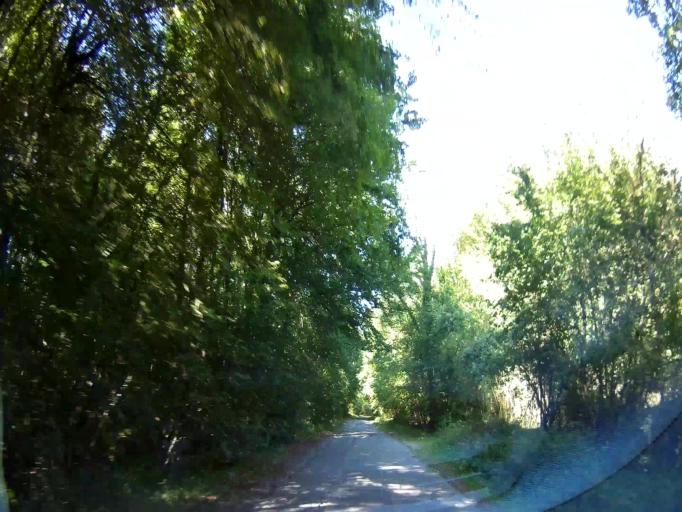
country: BE
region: Wallonia
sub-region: Province de Namur
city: Houyet
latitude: 50.2256
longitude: 4.9807
